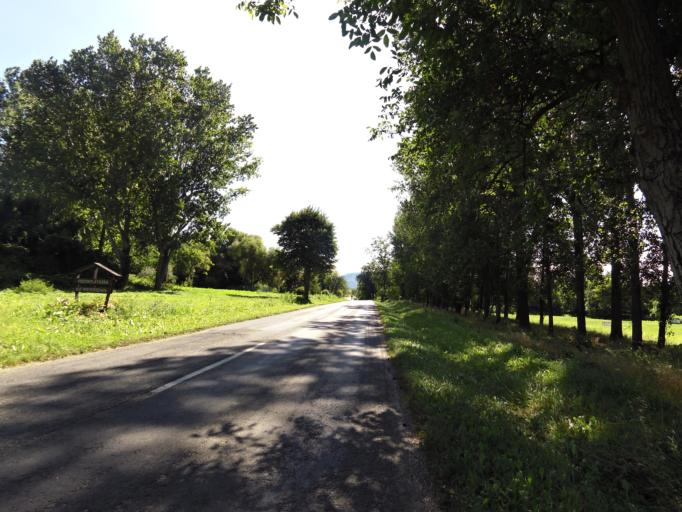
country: HU
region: Veszprem
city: Tapolca
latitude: 46.8320
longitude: 17.4362
